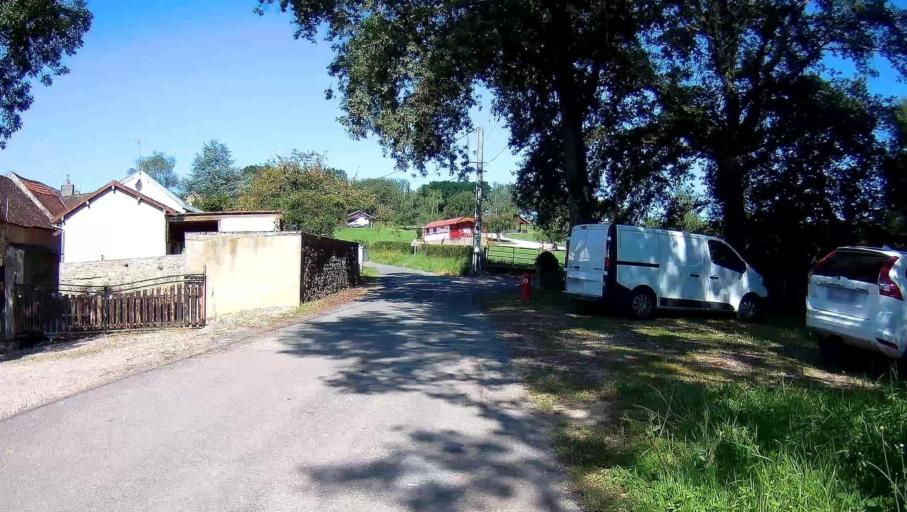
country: FR
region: Bourgogne
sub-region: Departement de Saone-et-Loire
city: Couches
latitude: 46.8431
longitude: 4.5755
